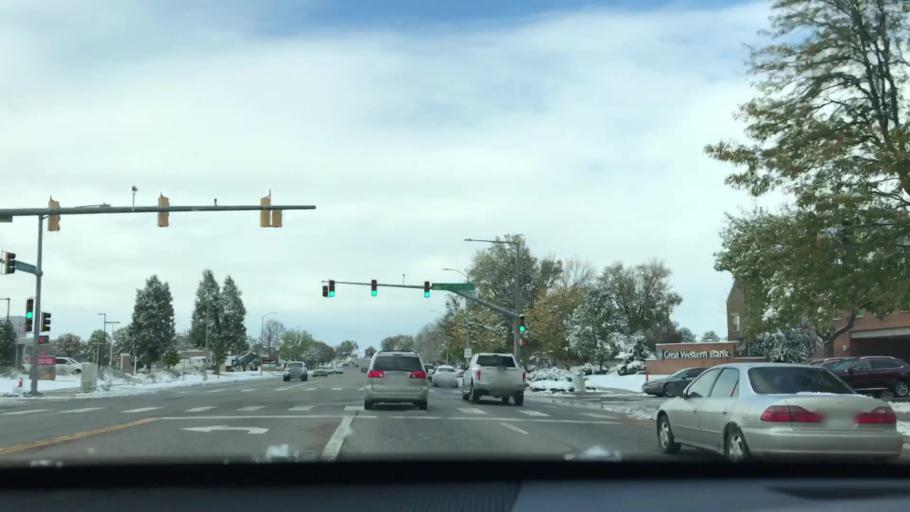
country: US
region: Colorado
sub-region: Boulder County
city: Longmont
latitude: 40.1955
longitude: -105.1024
